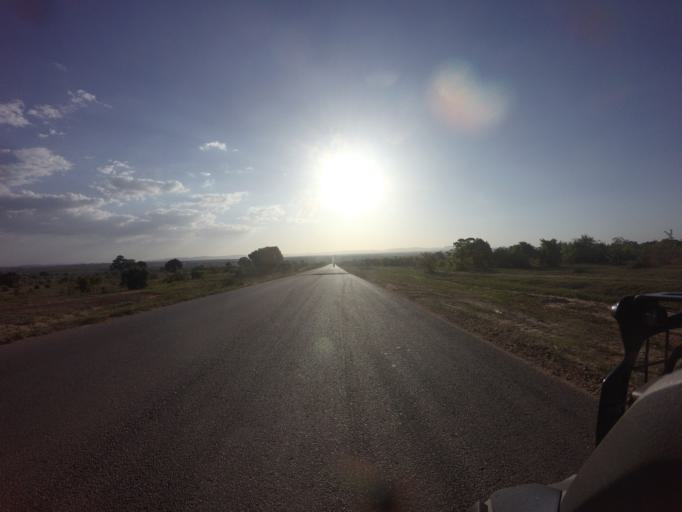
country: AO
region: Huila
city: Lubango
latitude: -14.7922
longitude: 13.6997
